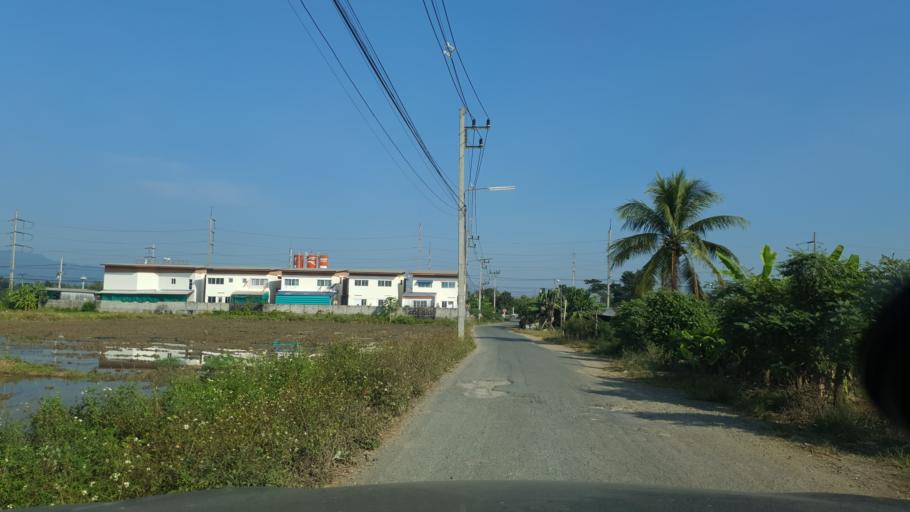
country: TH
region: Chiang Mai
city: Saraphi
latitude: 18.7183
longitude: 98.9938
